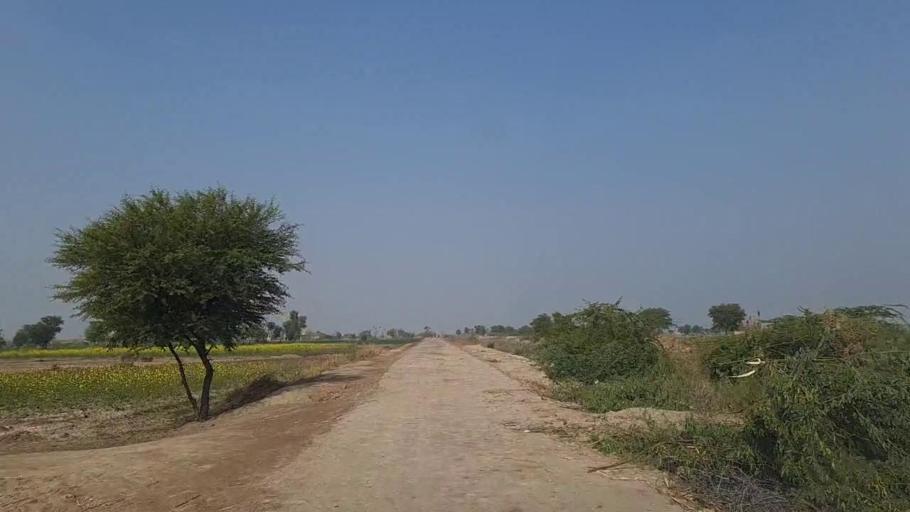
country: PK
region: Sindh
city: Nawabshah
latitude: 26.3657
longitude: 68.4272
